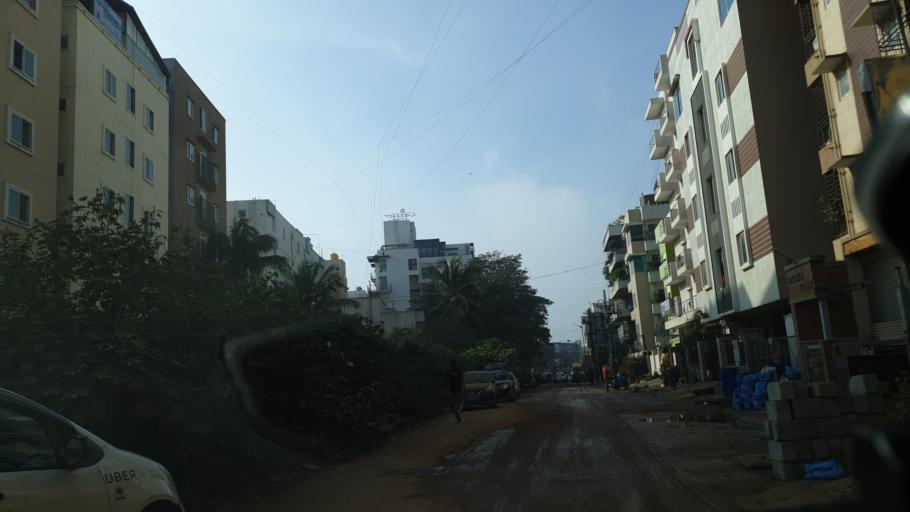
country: IN
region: Karnataka
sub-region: Bangalore Urban
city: Bangalore
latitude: 12.9587
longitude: 77.7086
